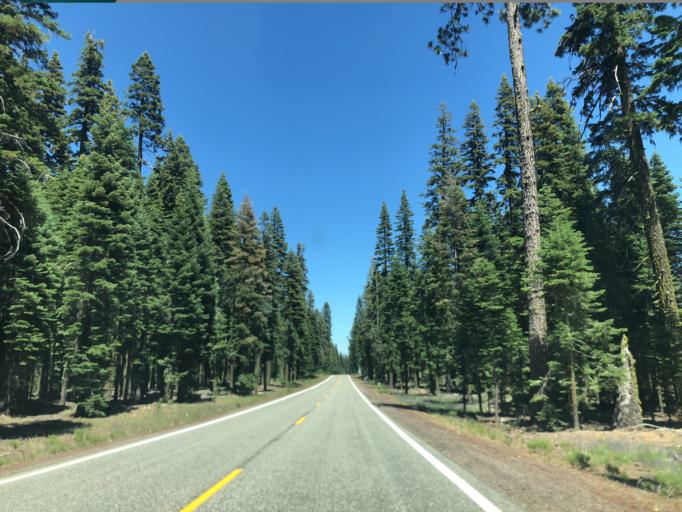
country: US
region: California
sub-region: Shasta County
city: Burney
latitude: 40.5853
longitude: -121.5524
